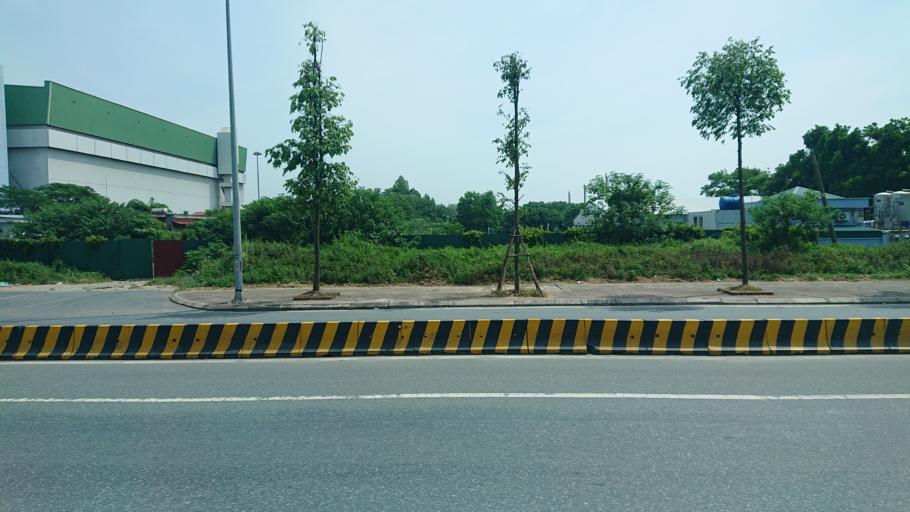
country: VN
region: Ha Noi
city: Soc Son
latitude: 21.2102
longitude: 105.8128
